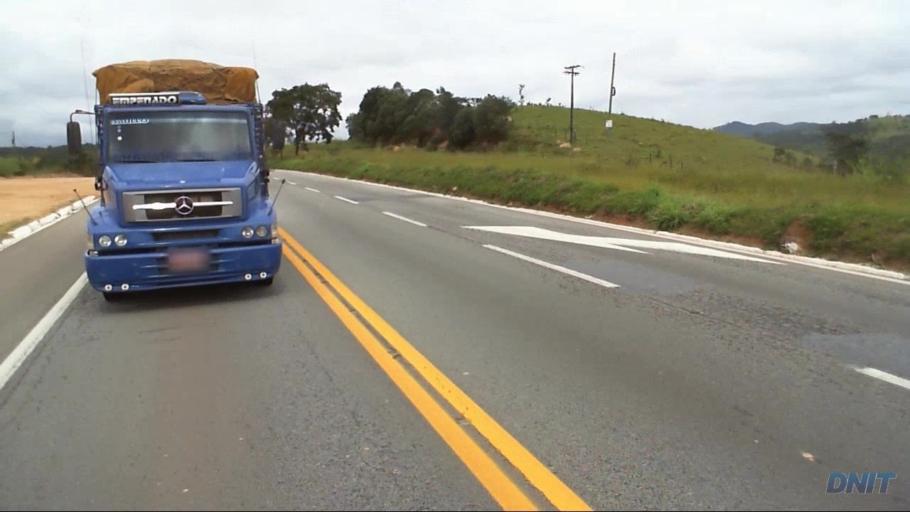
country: BR
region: Minas Gerais
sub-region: Caete
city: Caete
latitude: -19.7331
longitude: -43.5594
